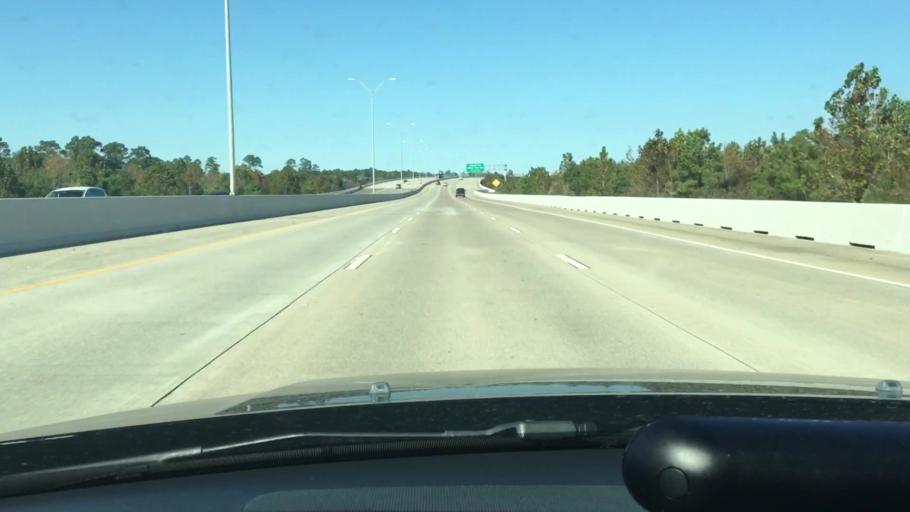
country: US
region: Texas
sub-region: Harris County
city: Sheldon
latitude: 29.8384
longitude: -95.1810
